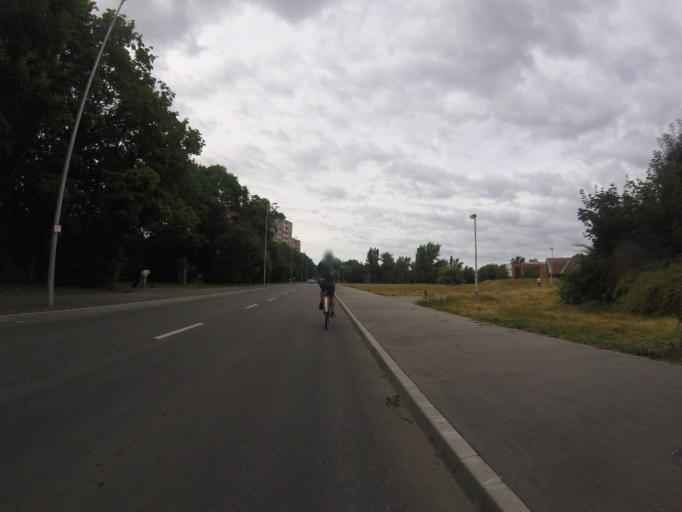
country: HU
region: Pest
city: Budakalasz
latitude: 47.6009
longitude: 19.0654
